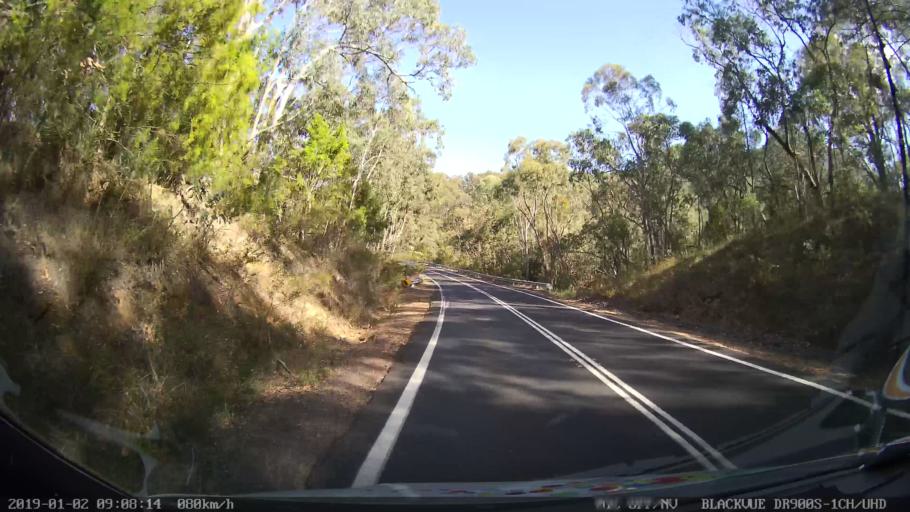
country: AU
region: New South Wales
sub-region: Tumut Shire
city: Tumut
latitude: -35.5321
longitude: 148.2941
